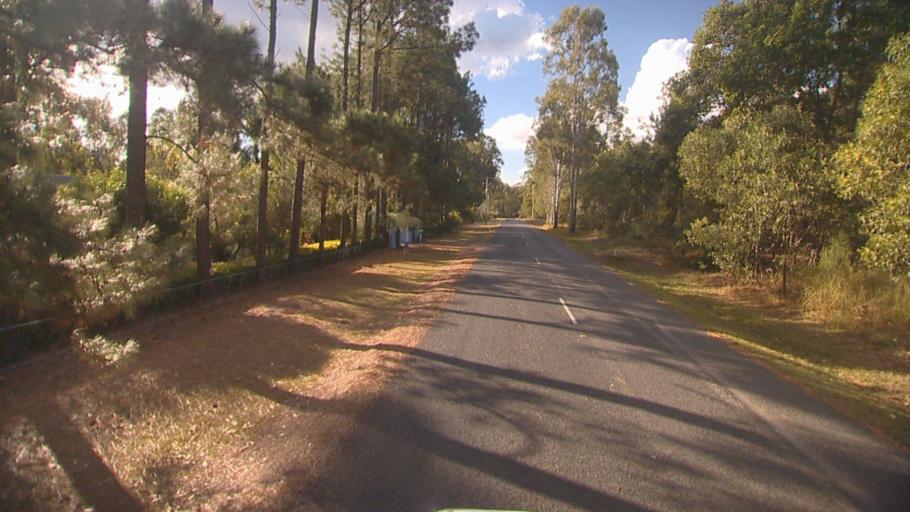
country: AU
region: Queensland
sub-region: Ipswich
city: Springfield Lakes
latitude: -27.6969
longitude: 152.9620
